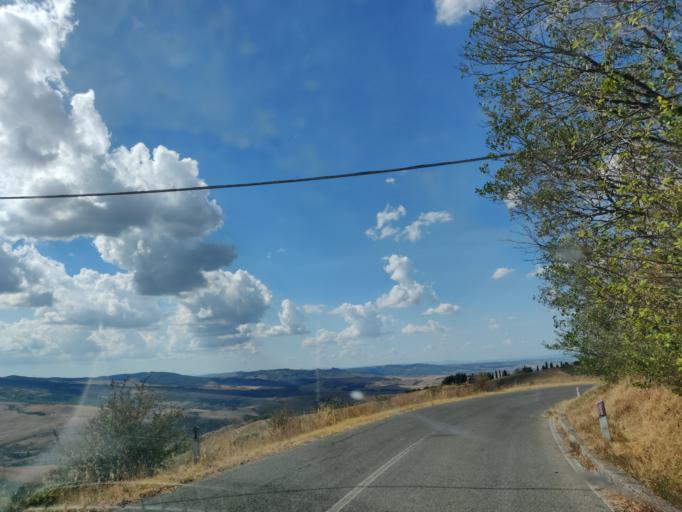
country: IT
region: Tuscany
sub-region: Provincia di Siena
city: Radicofani
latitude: 42.9499
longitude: 11.7308
